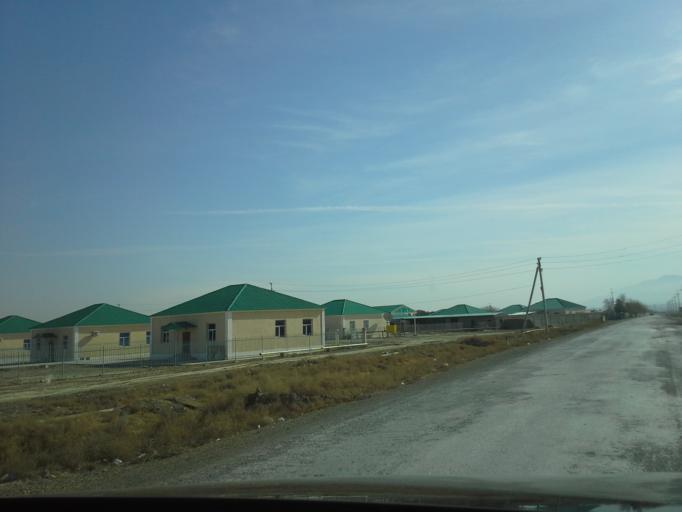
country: TM
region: Ahal
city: Arcabil
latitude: 38.1064
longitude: 57.9705
